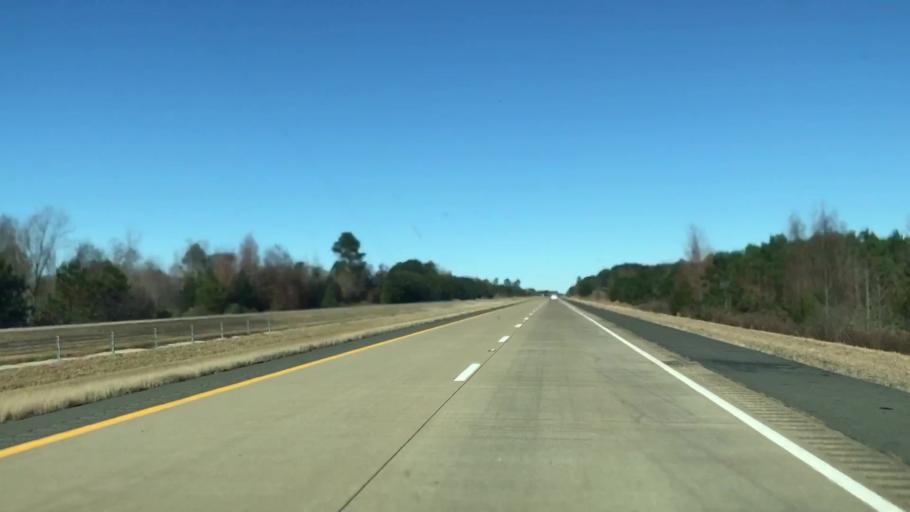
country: US
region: Texas
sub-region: Bowie County
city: Texarkana
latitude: 33.3025
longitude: -93.9314
